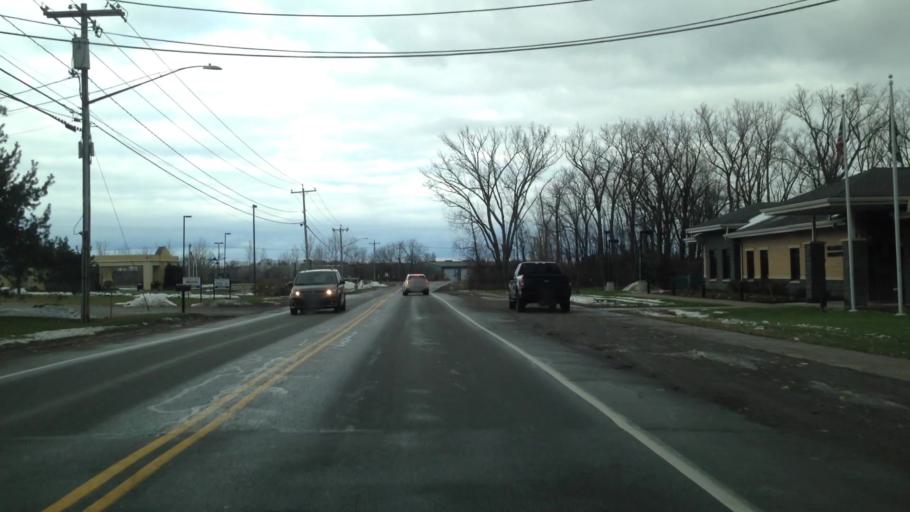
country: US
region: New York
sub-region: Genesee County
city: Batavia
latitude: 43.0147
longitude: -78.2000
